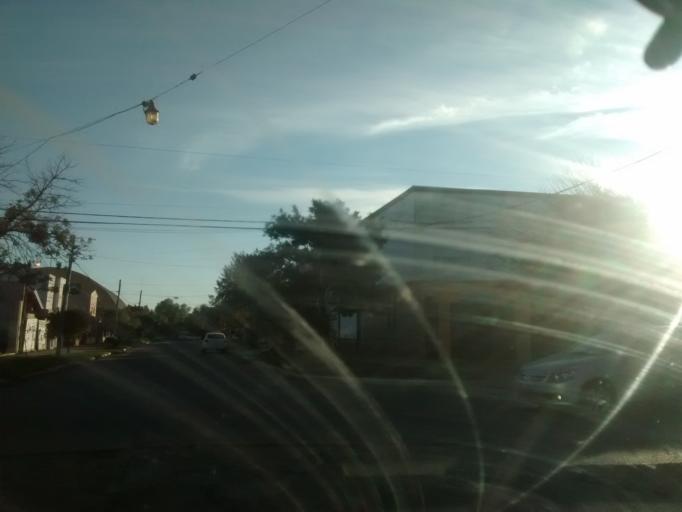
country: AR
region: Chaco
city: Resistencia
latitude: -27.4621
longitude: -58.9724
